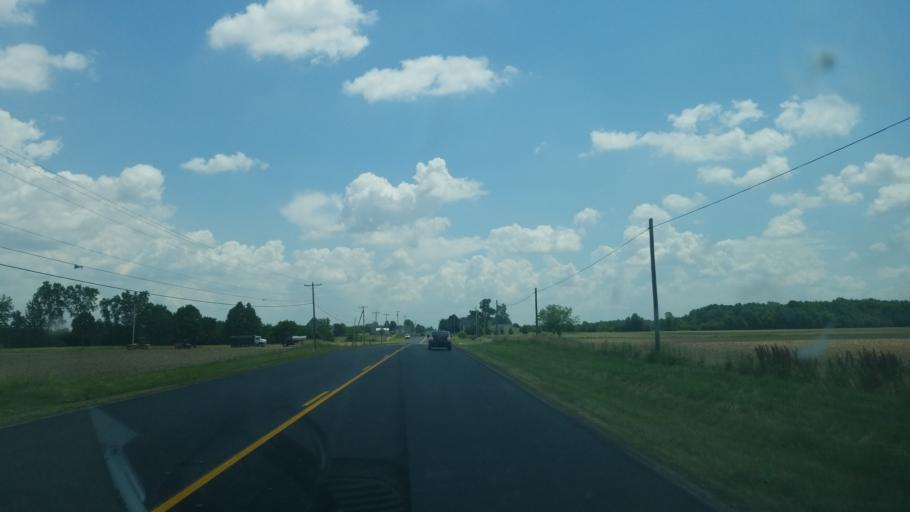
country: US
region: Ohio
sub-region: Hardin County
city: Ada
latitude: 40.7322
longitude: -83.9107
